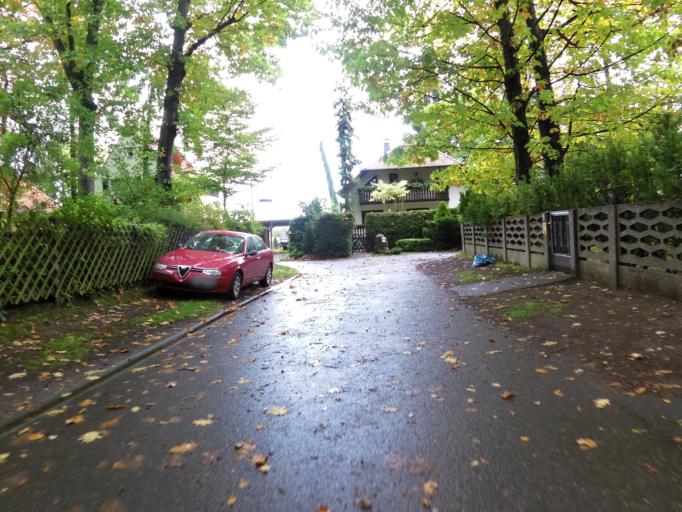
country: DE
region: Saxony
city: Grossposna
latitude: 51.3165
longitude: 12.4533
